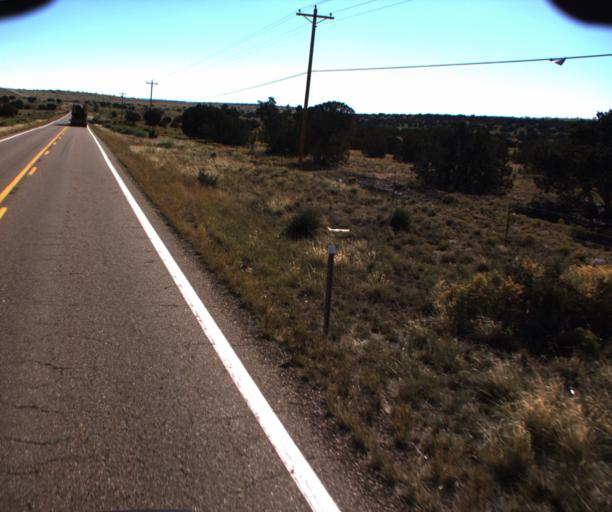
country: US
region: Arizona
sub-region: Apache County
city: Saint Johns
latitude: 34.4852
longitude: -109.5472
